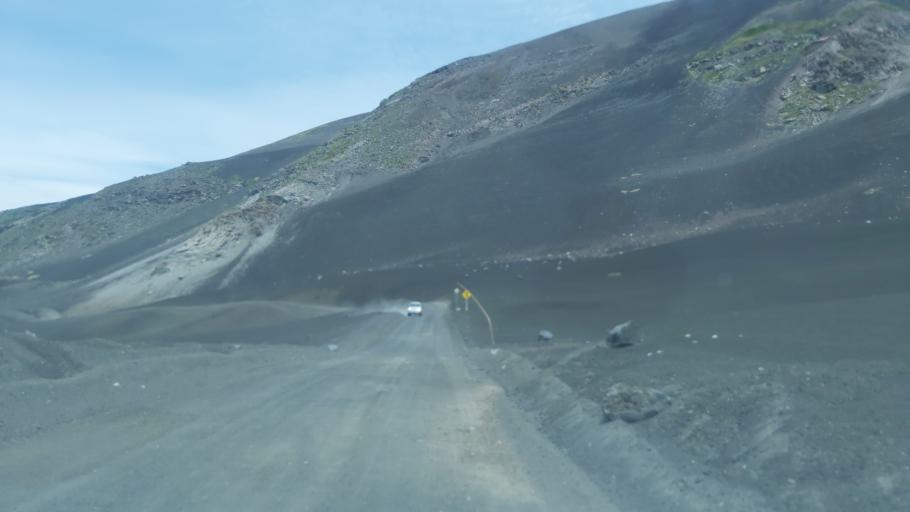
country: AR
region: Neuquen
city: Andacollo
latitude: -37.4024
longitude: -71.3021
